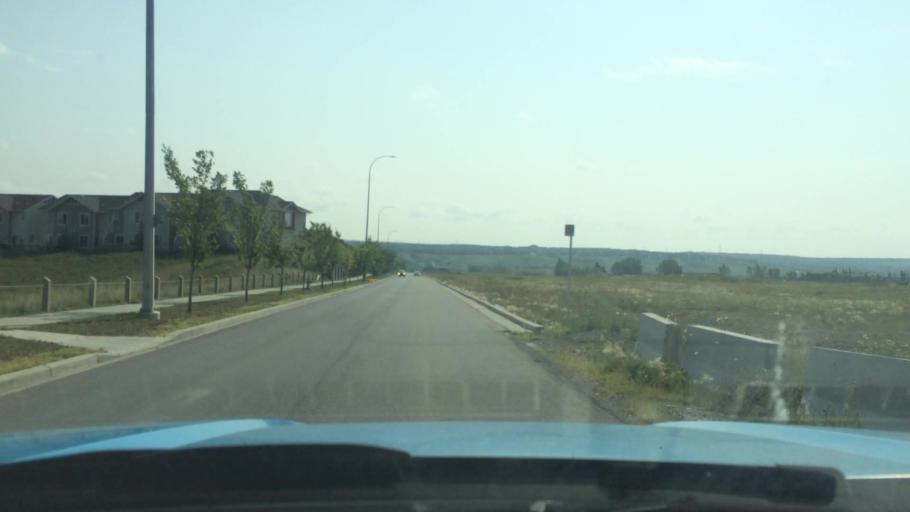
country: CA
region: Alberta
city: Calgary
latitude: 51.1759
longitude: -114.1499
